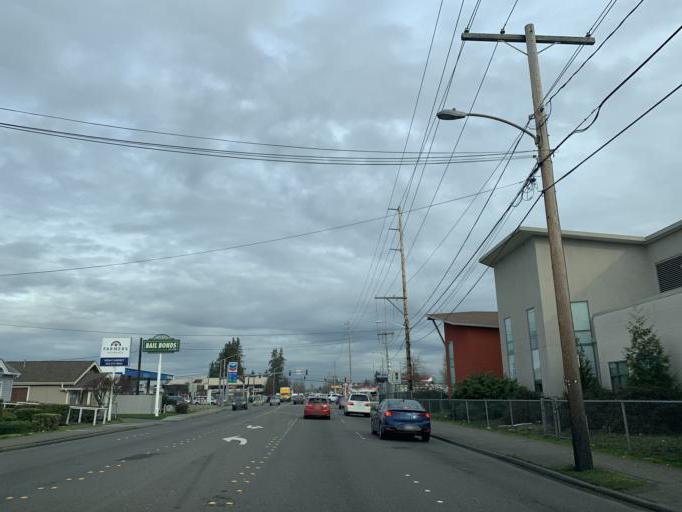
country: US
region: Washington
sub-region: King County
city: Kent
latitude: 47.3854
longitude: -122.2311
